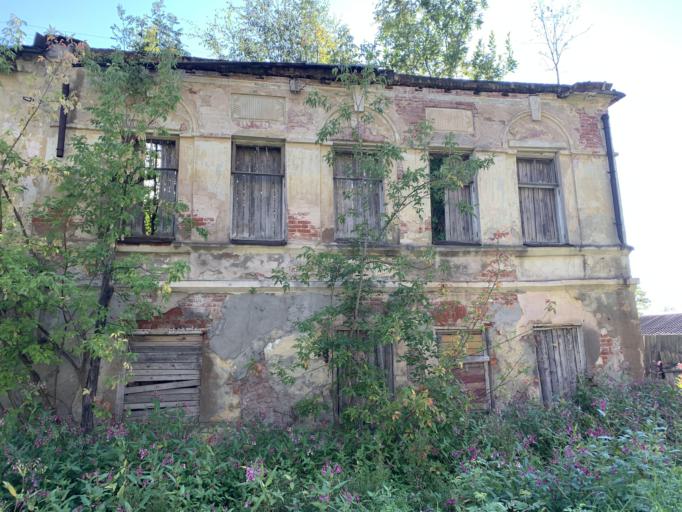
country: RU
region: Tverskaya
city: Vyshniy Volochek
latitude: 57.5871
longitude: 34.5473
